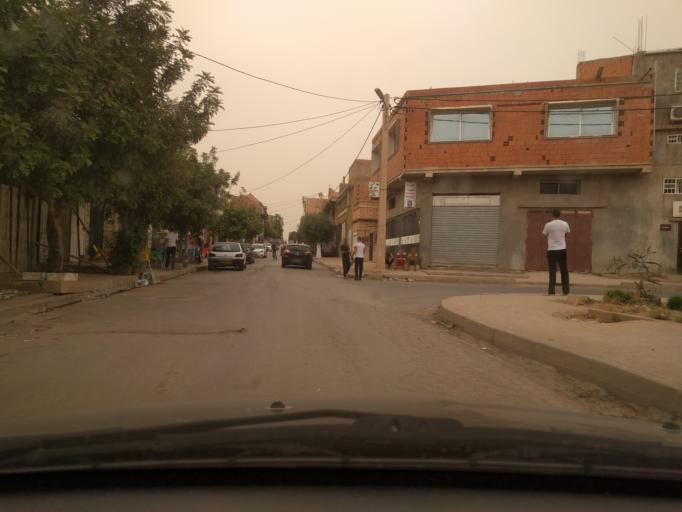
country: DZ
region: Tiaret
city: Frenda
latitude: 35.0647
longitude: 1.0627
